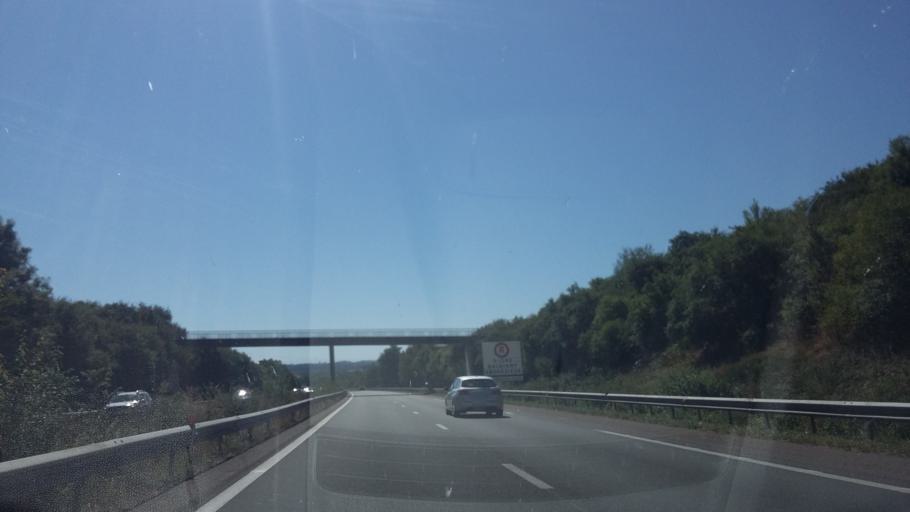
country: FR
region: Rhone-Alpes
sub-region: Departement de la Loire
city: Saint-Germain-Laval
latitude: 45.8335
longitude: 4.0986
